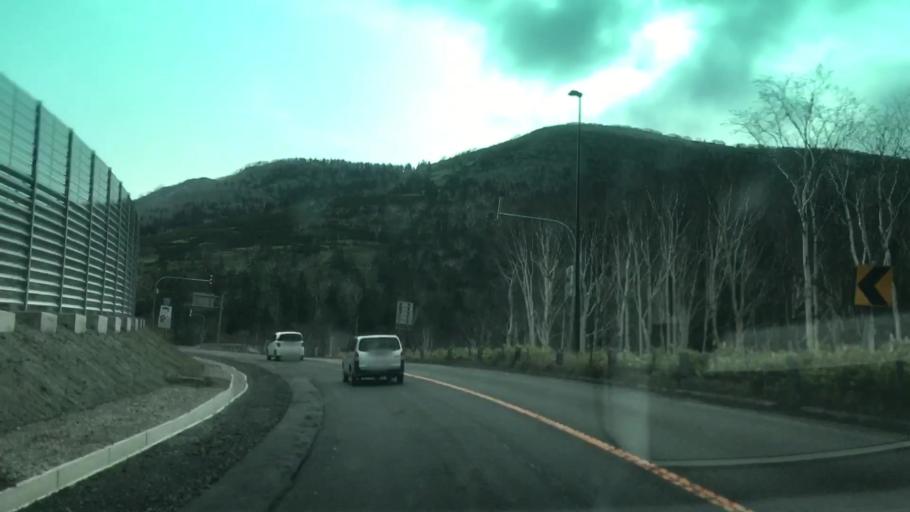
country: JP
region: Hokkaido
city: Otofuke
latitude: 42.9775
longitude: 142.7459
